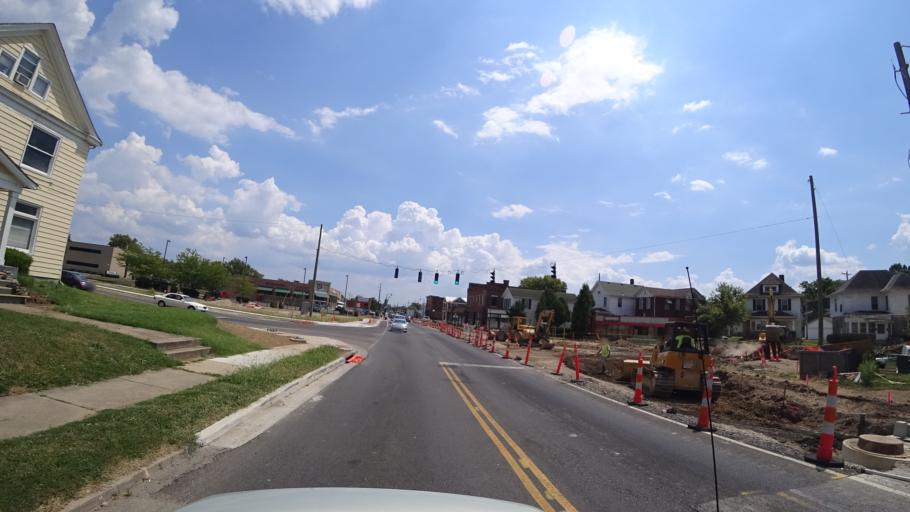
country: US
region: Ohio
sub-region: Butler County
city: Hamilton
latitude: 39.4074
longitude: -84.5742
